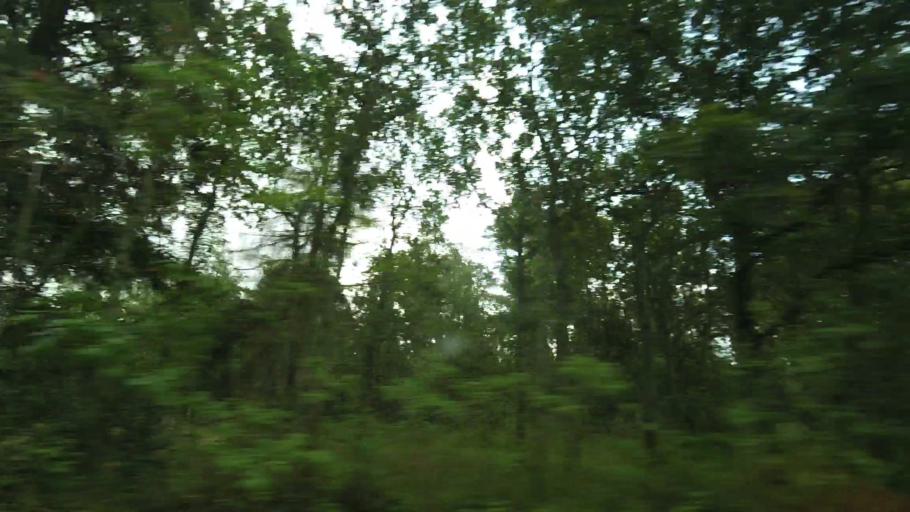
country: DK
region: Central Jutland
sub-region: Norddjurs Kommune
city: Allingabro
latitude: 56.4970
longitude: 10.3532
